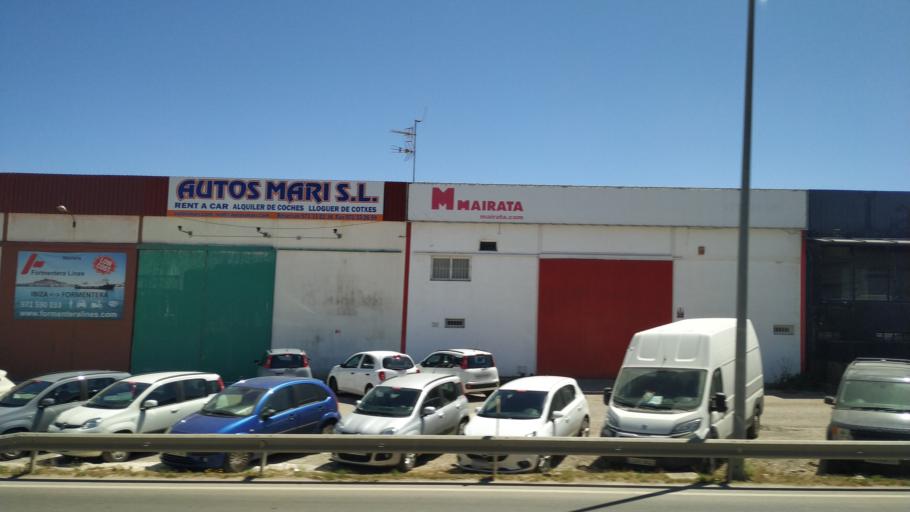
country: ES
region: Balearic Islands
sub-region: Illes Balears
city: Ibiza
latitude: 38.8823
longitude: 1.3793
